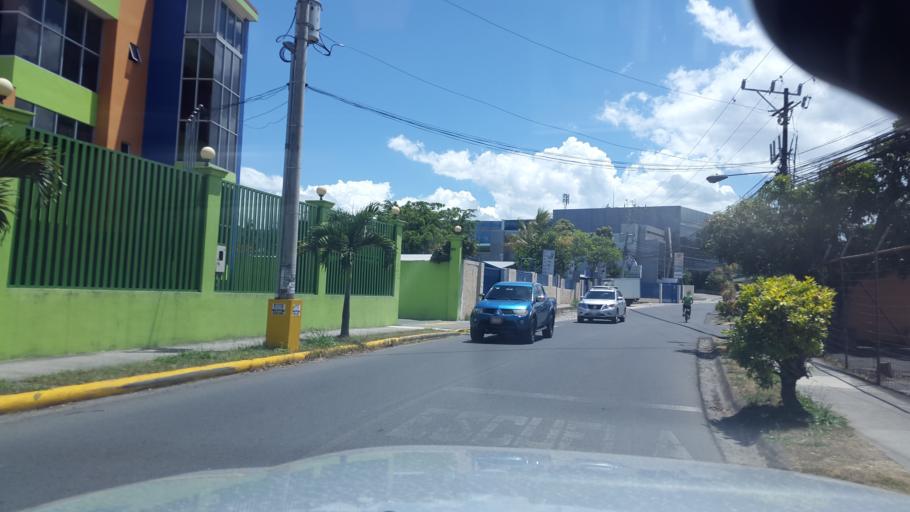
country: CR
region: San Jose
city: Curridabat
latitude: 9.9157
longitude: -84.0277
